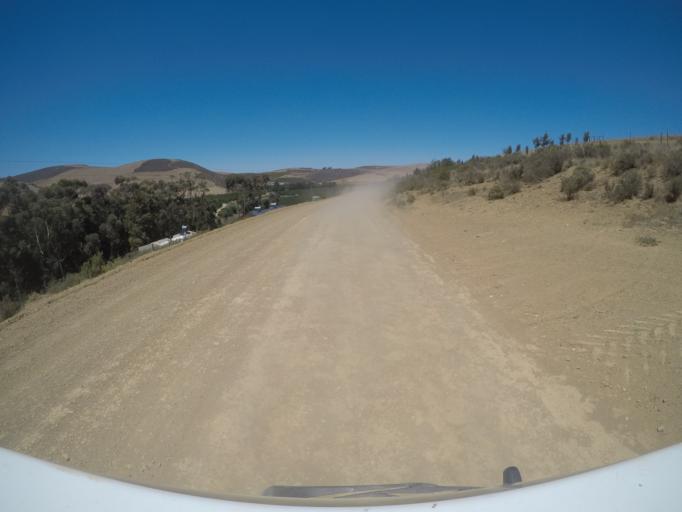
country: ZA
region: Western Cape
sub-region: Overberg District Municipality
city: Grabouw
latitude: -34.1047
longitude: 19.2092
